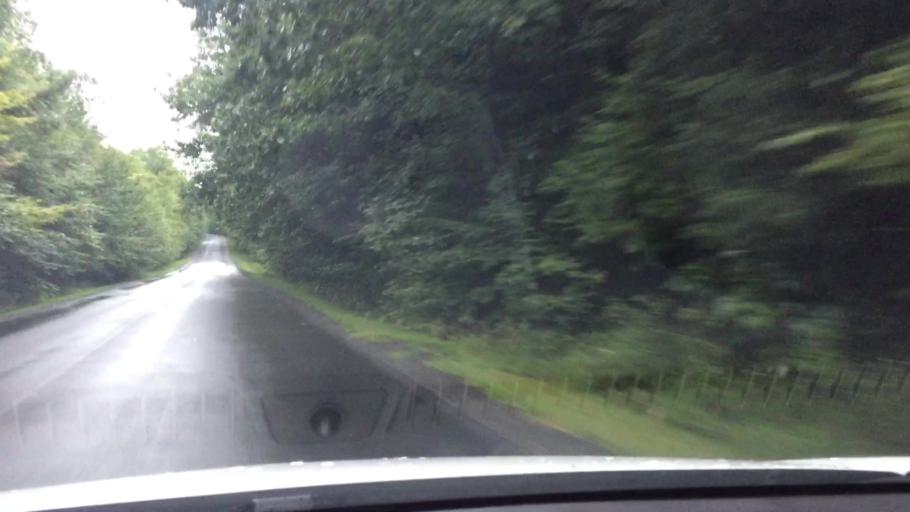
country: US
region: Massachusetts
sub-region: Berkshire County
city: Otis
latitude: 42.1459
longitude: -73.0539
